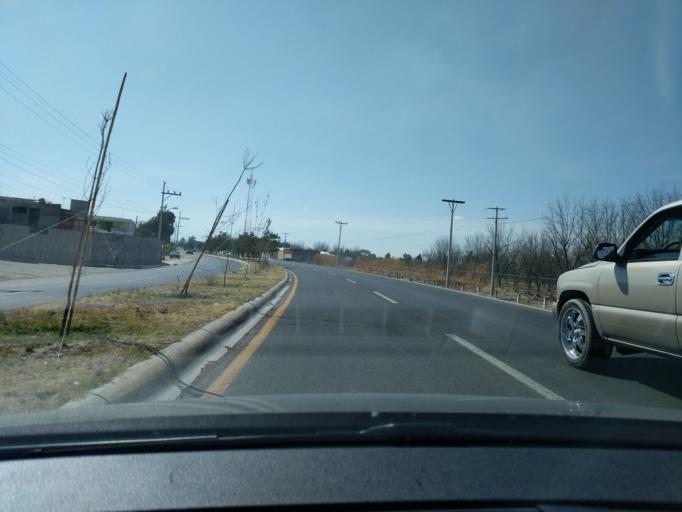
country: MX
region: Durango
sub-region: Durango
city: Sebastian Lerdo de Tejada
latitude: 23.9815
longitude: -104.5932
